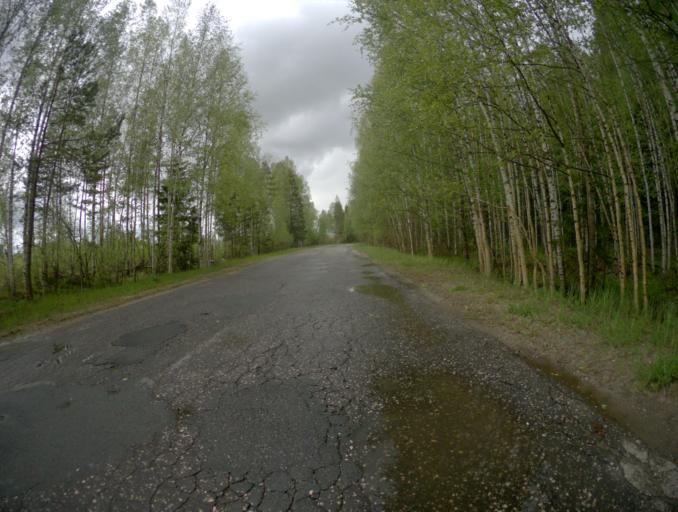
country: RU
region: Vladimir
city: Velikodvorskiy
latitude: 55.3540
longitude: 40.9087
